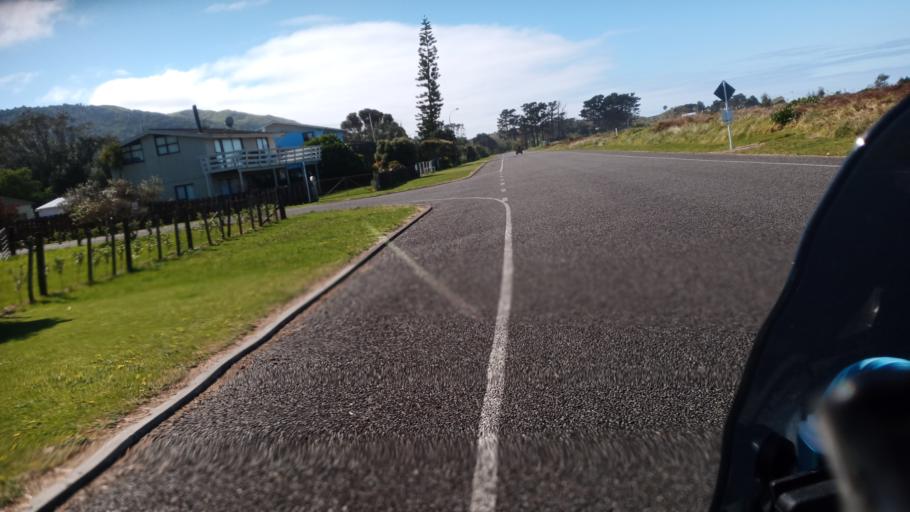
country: NZ
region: Gisborne
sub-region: Gisborne District
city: Gisborne
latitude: -39.0175
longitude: 177.8845
